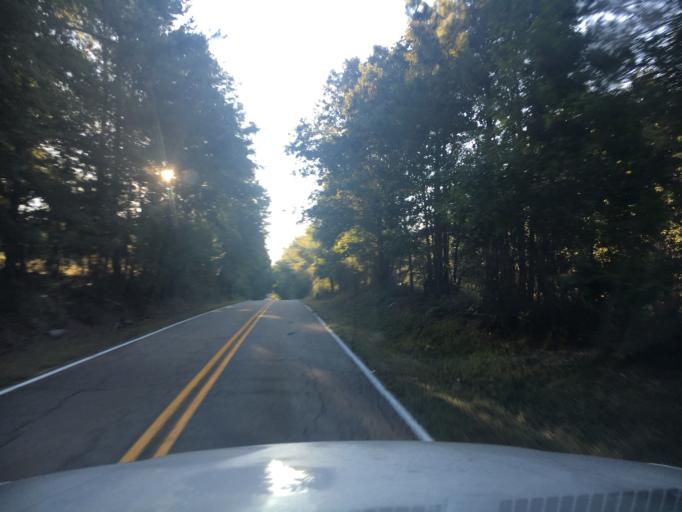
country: US
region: South Carolina
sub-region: Spartanburg County
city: Woodruff
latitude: 34.7764
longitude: -81.9762
